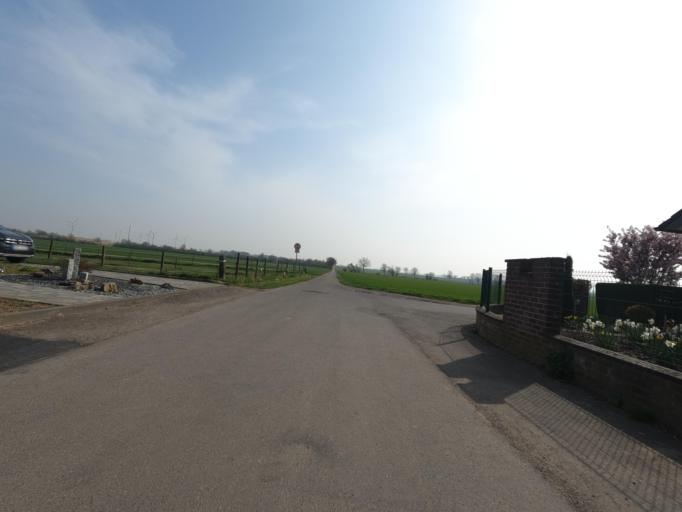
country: DE
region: North Rhine-Westphalia
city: Erkelenz
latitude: 51.0583
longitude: 6.3536
